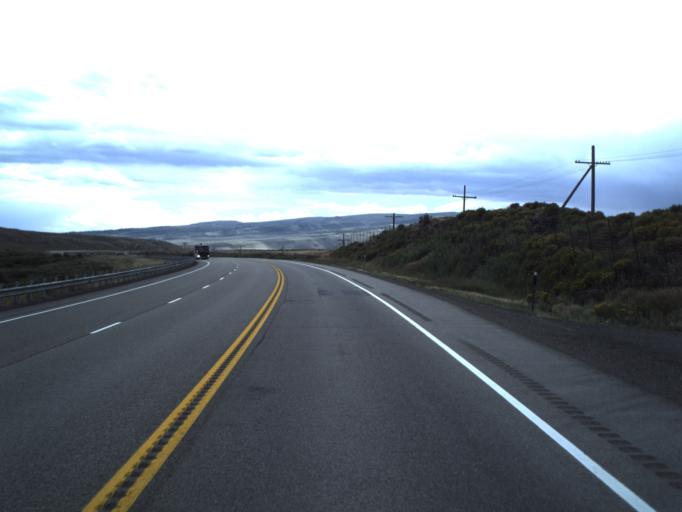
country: US
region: Utah
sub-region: Carbon County
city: Helper
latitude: 39.8853
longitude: -111.0491
